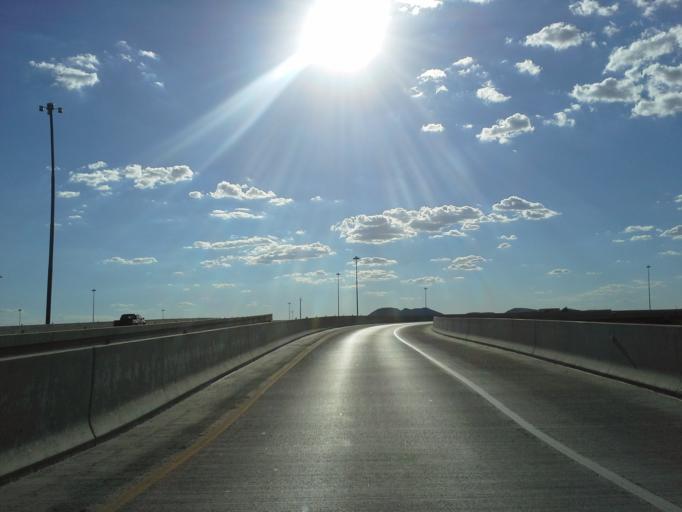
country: US
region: Arizona
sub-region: Maricopa County
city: Glendale
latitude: 33.6693
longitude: -112.1094
